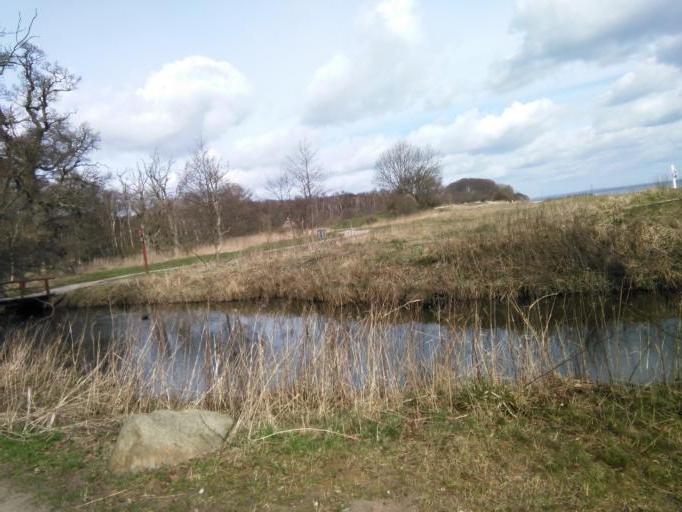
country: DK
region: Central Jutland
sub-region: Arhus Kommune
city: Beder
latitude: 56.0853
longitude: 10.2485
